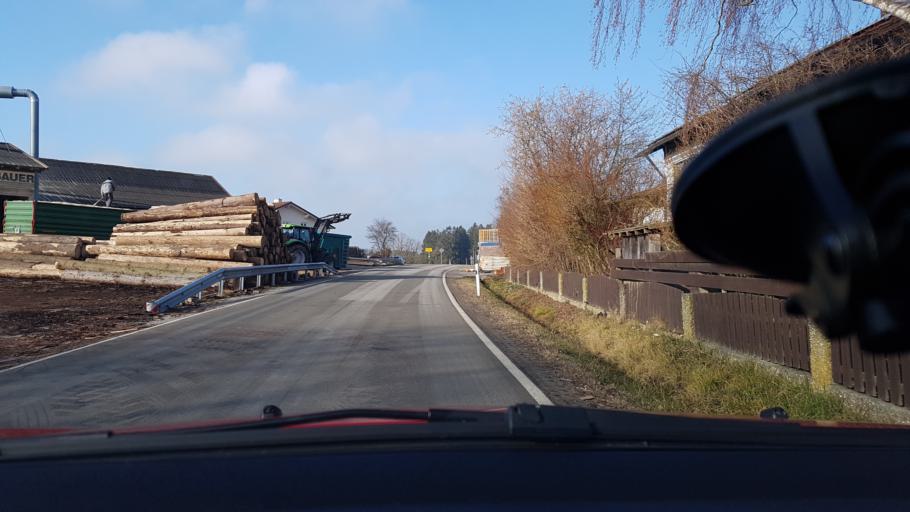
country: DE
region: Bavaria
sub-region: Lower Bavaria
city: Wittibreut
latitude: 48.3300
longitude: 12.9821
